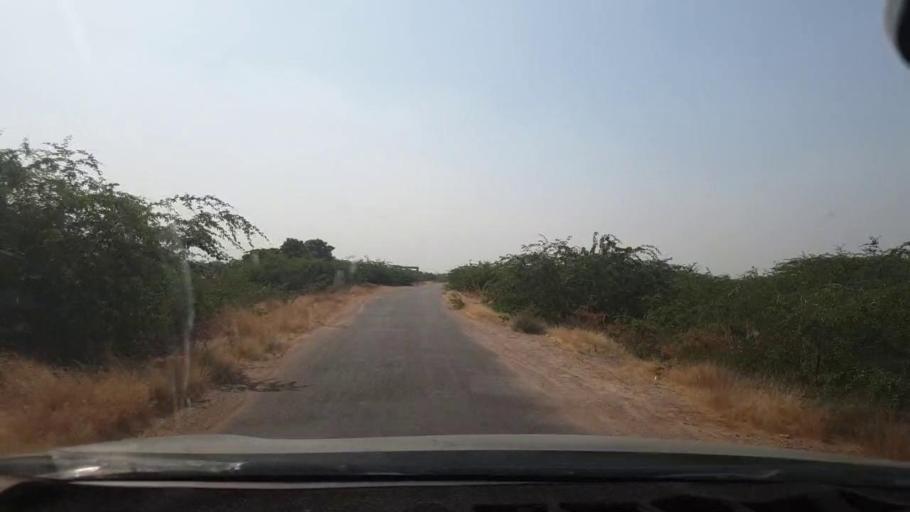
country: PK
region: Sindh
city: Malir Cantonment
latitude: 25.1021
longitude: 67.1957
